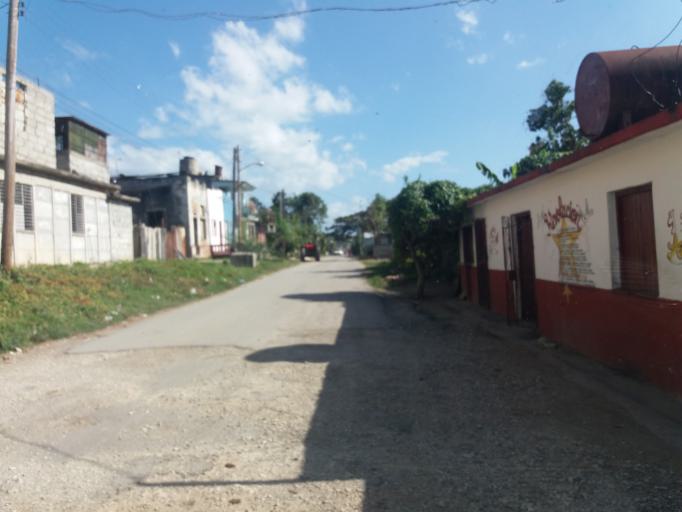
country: CU
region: Cienfuegos
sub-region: Municipio de Cienfuegos
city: Cienfuegos
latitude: 22.1534
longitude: -80.4325
